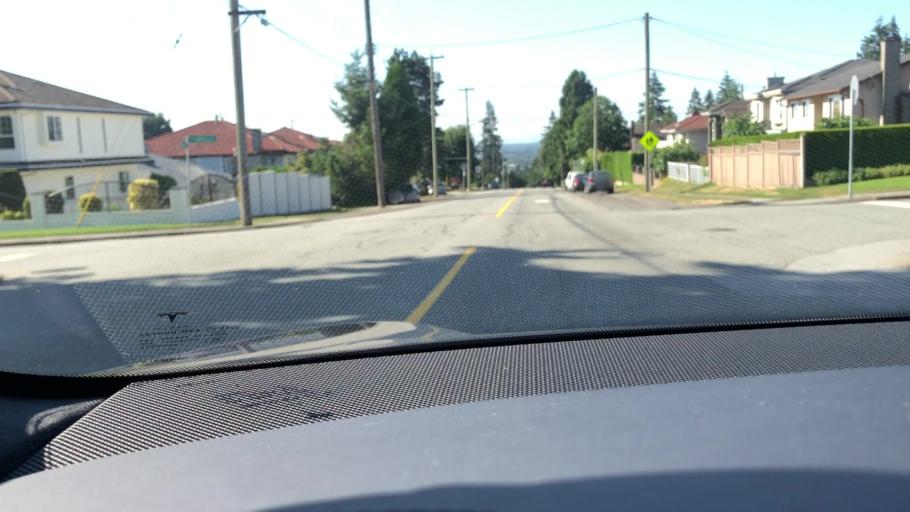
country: CA
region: British Columbia
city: Burnaby
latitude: 49.2140
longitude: -122.9720
